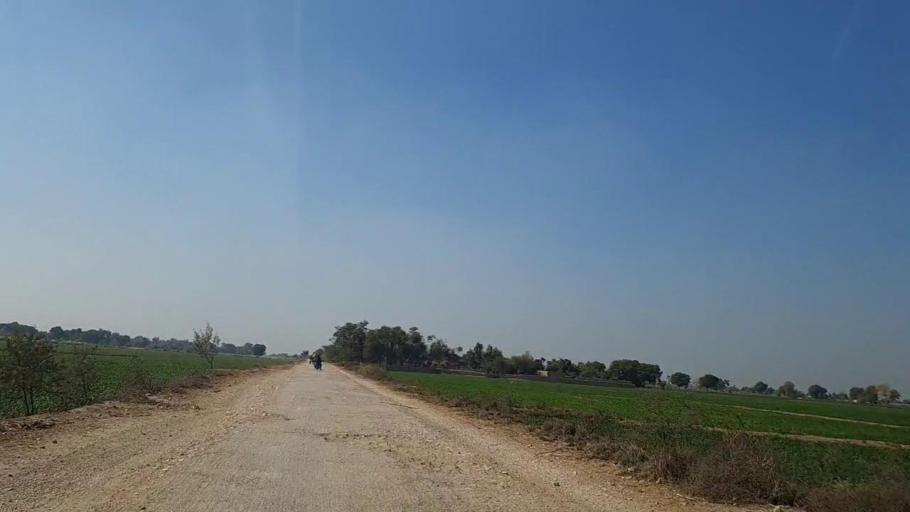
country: PK
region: Sindh
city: Daulatpur
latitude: 26.2906
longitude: 68.0854
